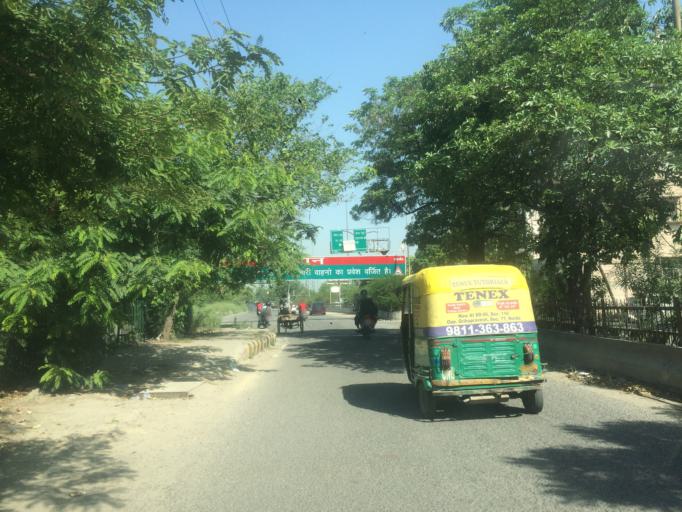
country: IN
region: Uttar Pradesh
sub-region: Gautam Buddha Nagar
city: Noida
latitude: 28.5756
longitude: 77.3686
